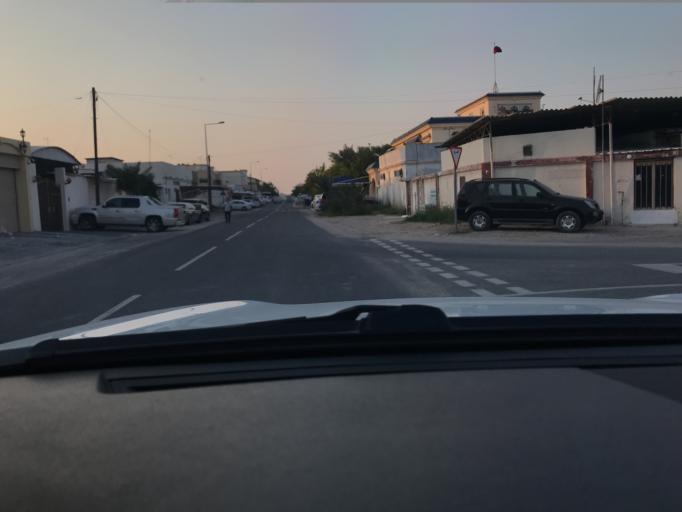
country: QA
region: Baladiyat ad Dawhah
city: Doha
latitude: 25.2518
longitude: 51.5060
